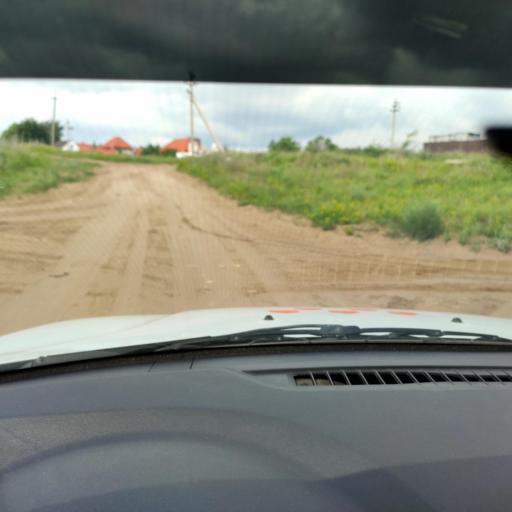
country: RU
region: Samara
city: Podstepki
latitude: 53.6140
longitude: 49.0327
